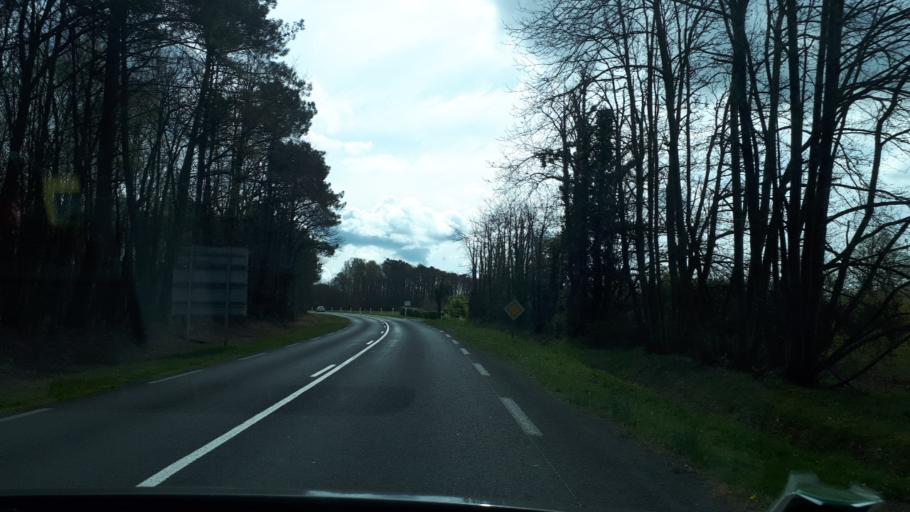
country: FR
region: Pays de la Loire
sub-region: Departement de la Sarthe
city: Le Grand-Luce
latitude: 47.8762
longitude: 0.4316
